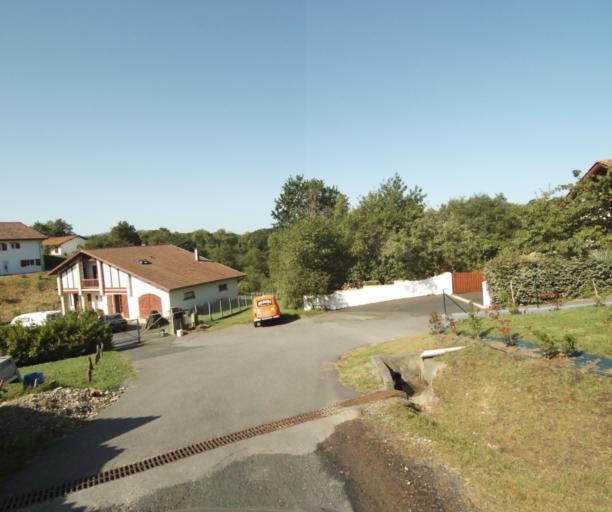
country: FR
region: Aquitaine
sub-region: Departement des Pyrenees-Atlantiques
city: Mouguerre
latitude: 43.4714
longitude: -1.4508
